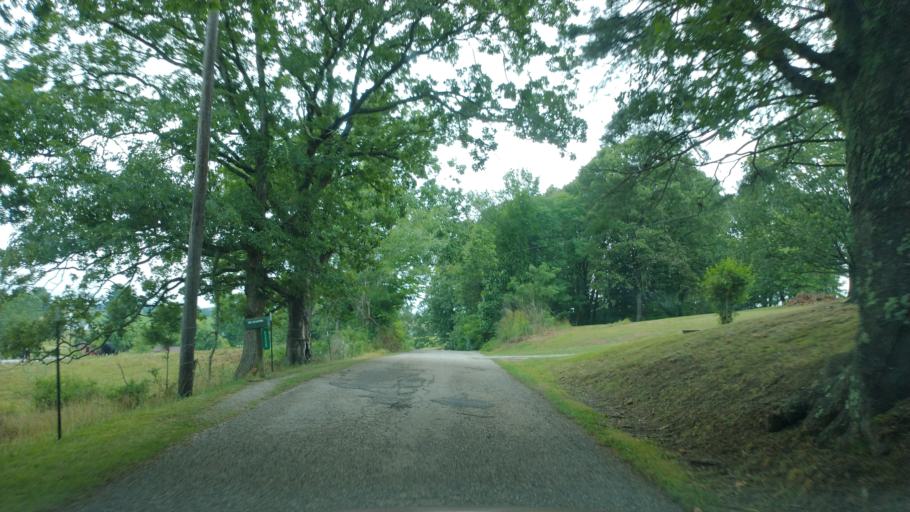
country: US
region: West Virginia
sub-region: Mason County
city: New Haven
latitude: 38.9250
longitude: -81.9557
